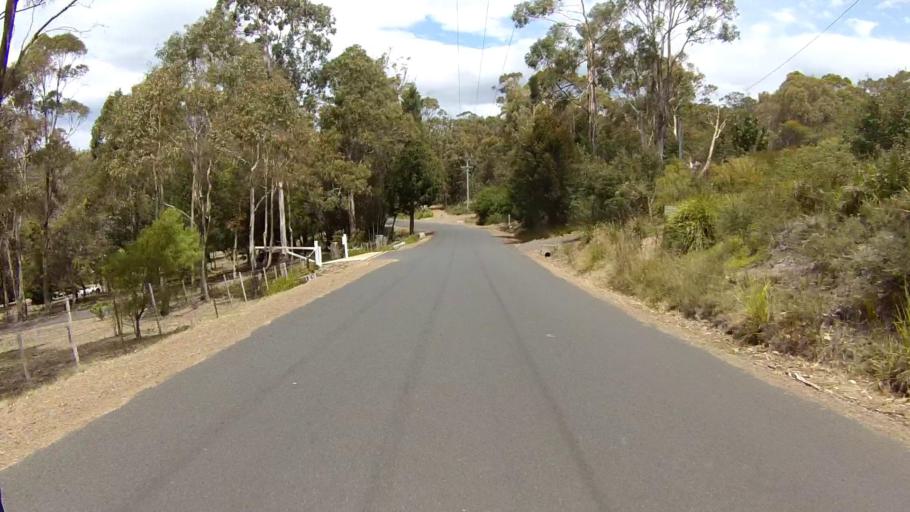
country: AU
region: Tasmania
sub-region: Sorell
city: Sorell
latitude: -42.5894
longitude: 147.9149
